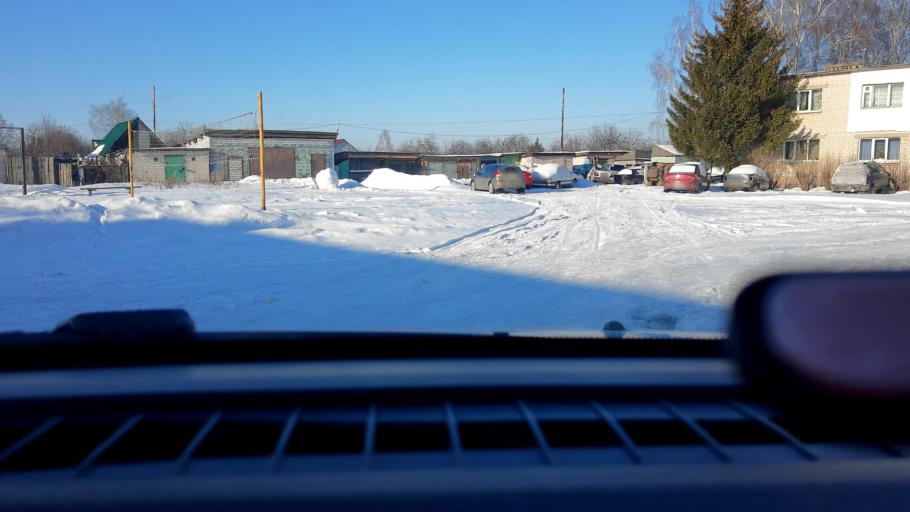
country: RU
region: Nizjnij Novgorod
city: Burevestnik
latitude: 56.1405
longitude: 43.9220
